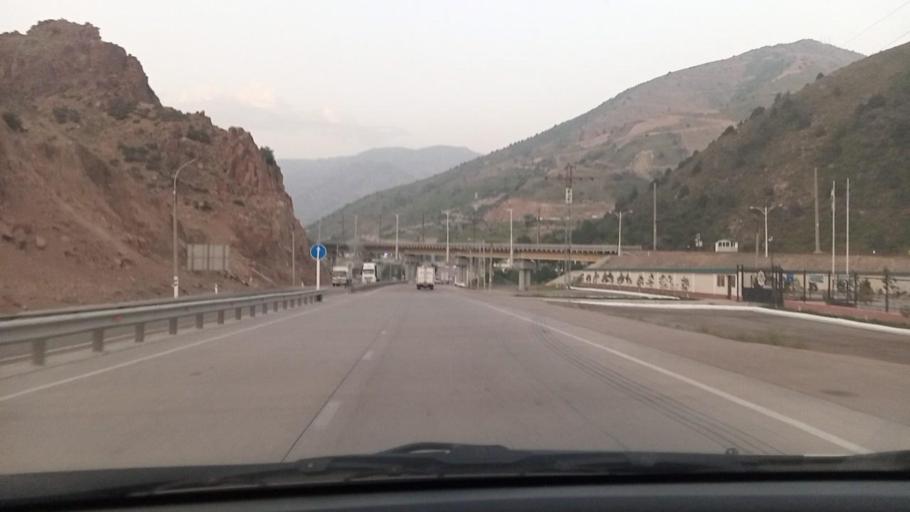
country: UZ
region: Toshkent
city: Angren
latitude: 41.1515
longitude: 70.4340
